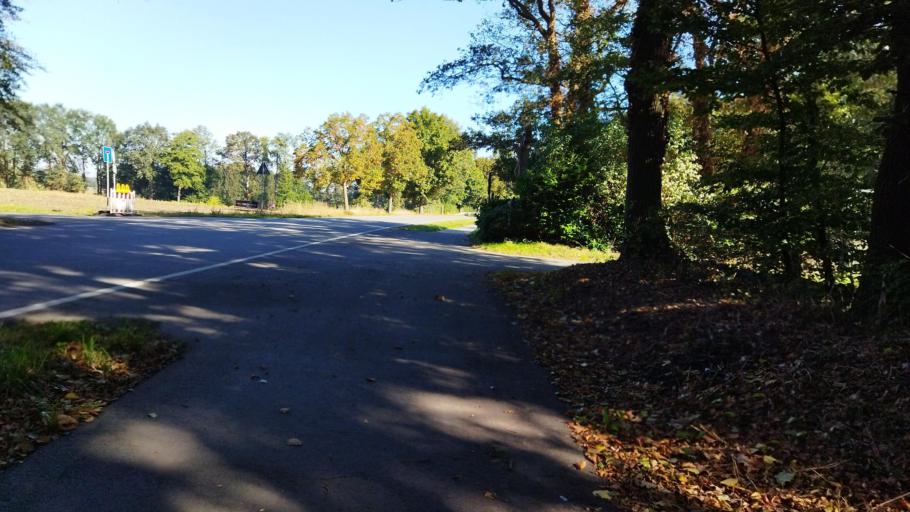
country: DE
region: North Rhine-Westphalia
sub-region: Regierungsbezirk Munster
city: Wettringen
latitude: 52.2428
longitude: 7.3113
